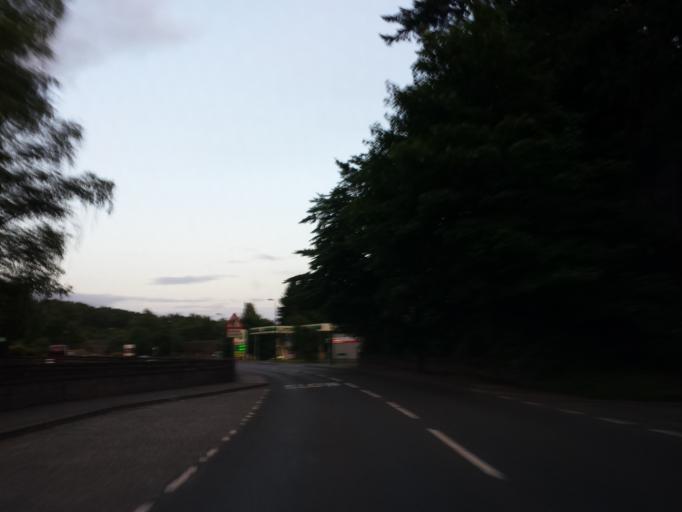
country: GB
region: Scotland
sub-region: Perth and Kinross
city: Pitlochry
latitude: 56.6981
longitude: -3.7230
